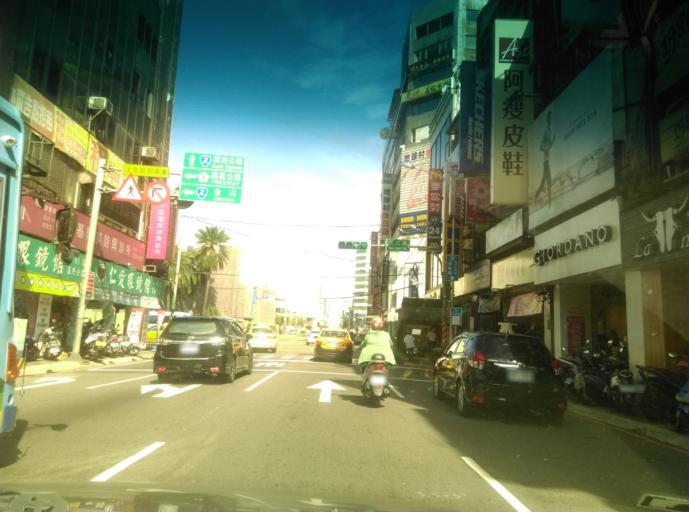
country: TW
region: Taiwan
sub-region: Keelung
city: Keelung
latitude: 25.1291
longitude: 121.7431
